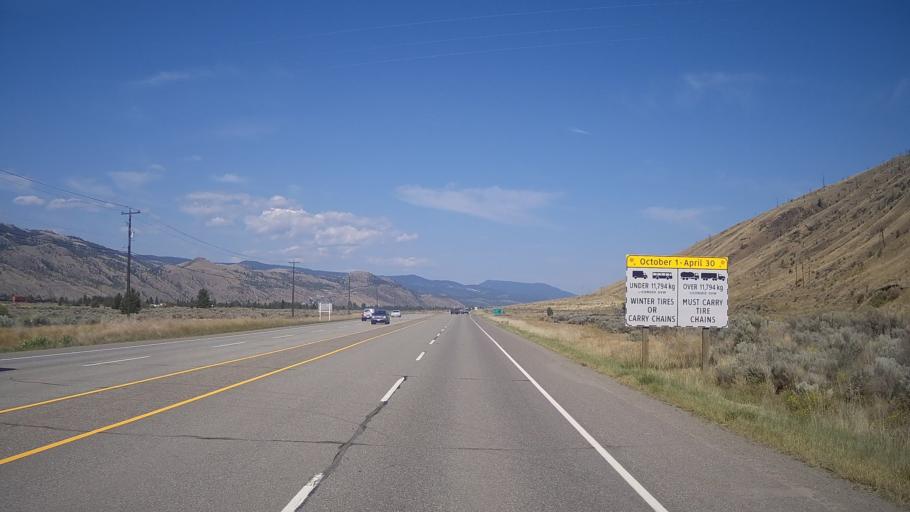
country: CA
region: British Columbia
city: Kamloops
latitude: 50.7348
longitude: -120.3374
